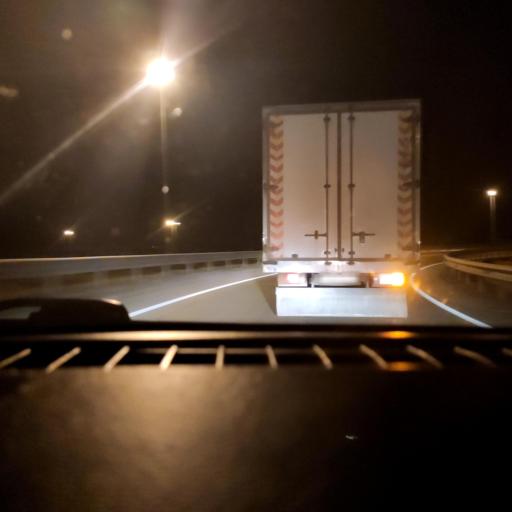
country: RU
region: Perm
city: Froly
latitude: 57.9339
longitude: 56.2706
